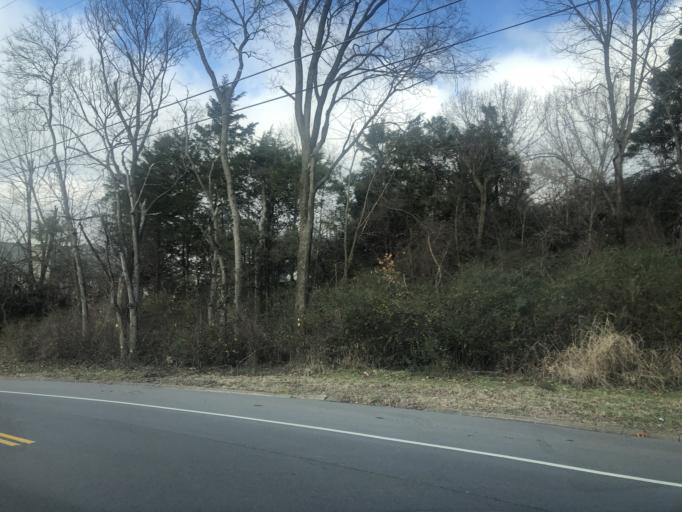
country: US
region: Tennessee
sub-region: Rutherford County
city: La Vergne
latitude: 36.0841
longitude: -86.6581
